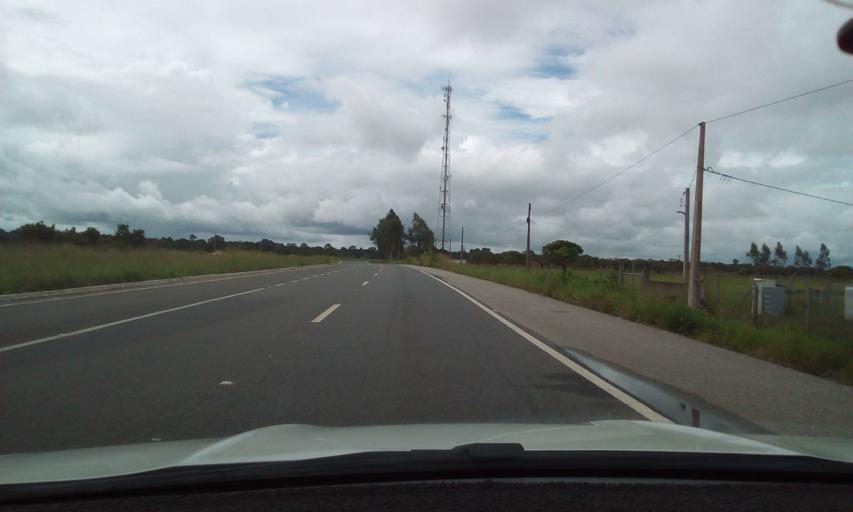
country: BR
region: Paraiba
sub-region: Cruz Do Espirito Santo
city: Cruz do Espirito Santo
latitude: -7.2035
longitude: -35.1160
